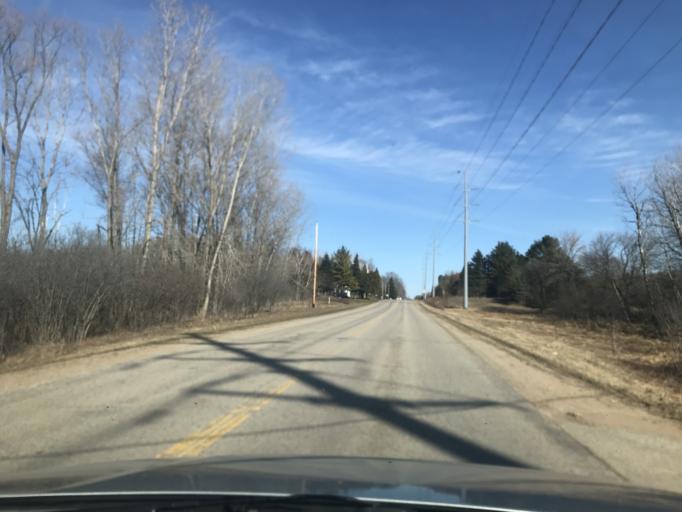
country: US
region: Wisconsin
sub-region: Marinette County
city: Marinette
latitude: 45.1450
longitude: -87.6493
